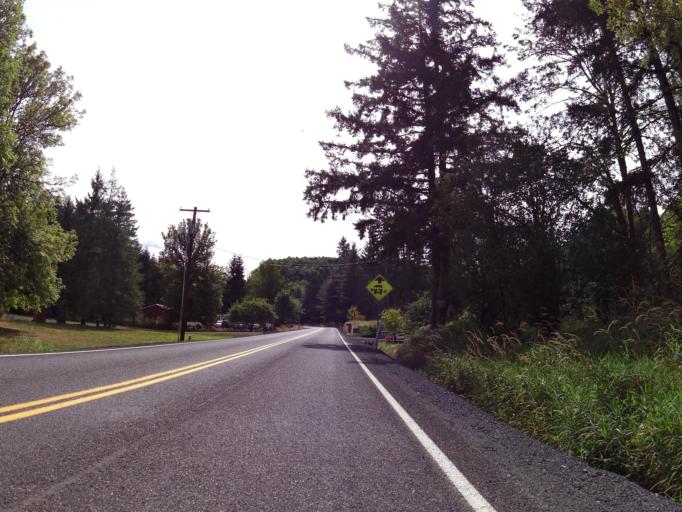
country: US
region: Washington
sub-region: Lewis County
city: Napavine
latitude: 46.5639
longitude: -122.9657
